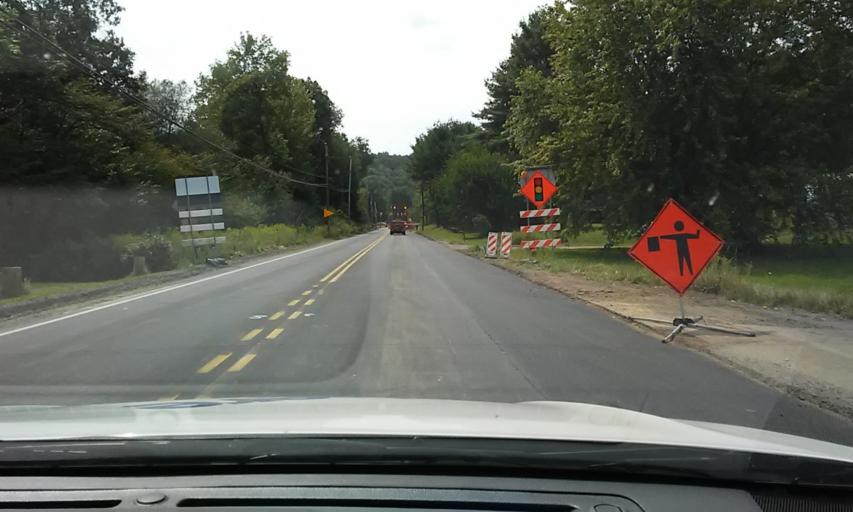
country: US
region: Pennsylvania
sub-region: Clearfield County
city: Treasure Lake
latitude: 41.1876
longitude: -78.6035
